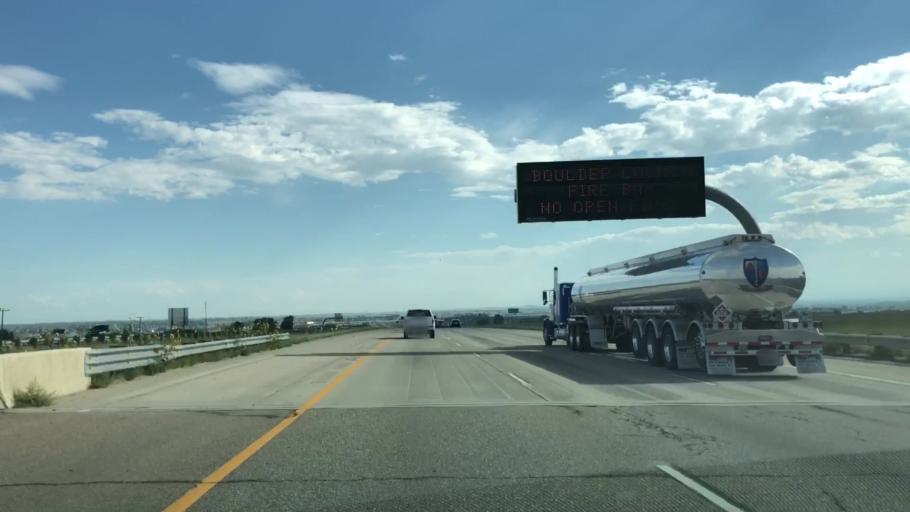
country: US
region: Colorado
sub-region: Weld County
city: Mead
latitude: 40.1895
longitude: -104.9808
